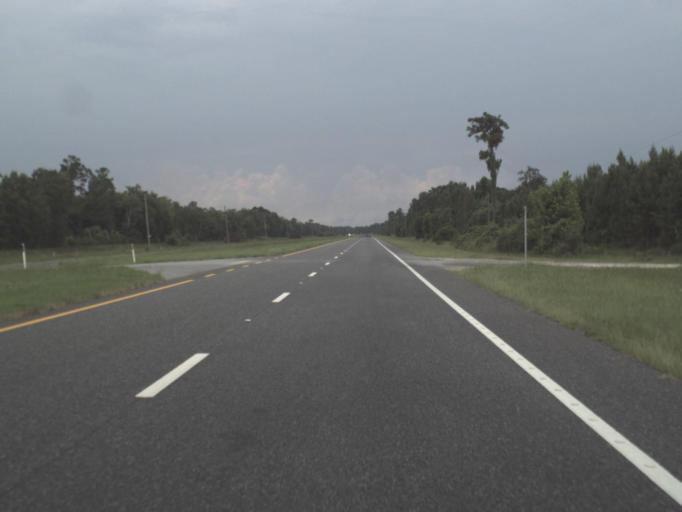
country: US
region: Florida
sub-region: Levy County
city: Inglis
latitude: 29.2054
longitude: -82.6942
